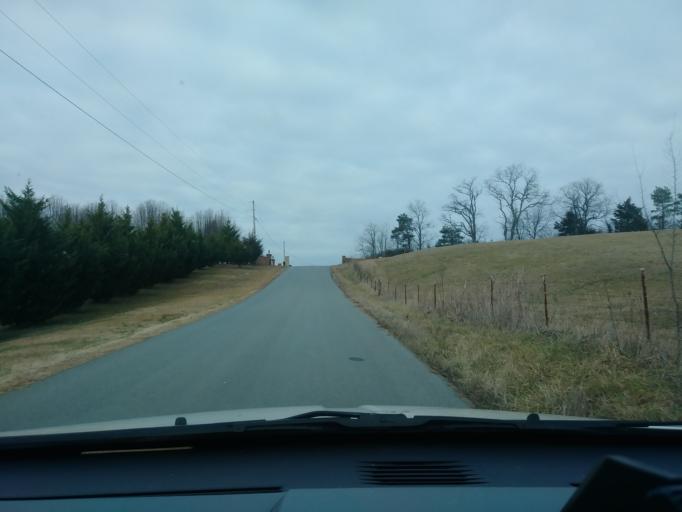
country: US
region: Tennessee
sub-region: Greene County
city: Mosheim
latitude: 36.1066
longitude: -82.9129
